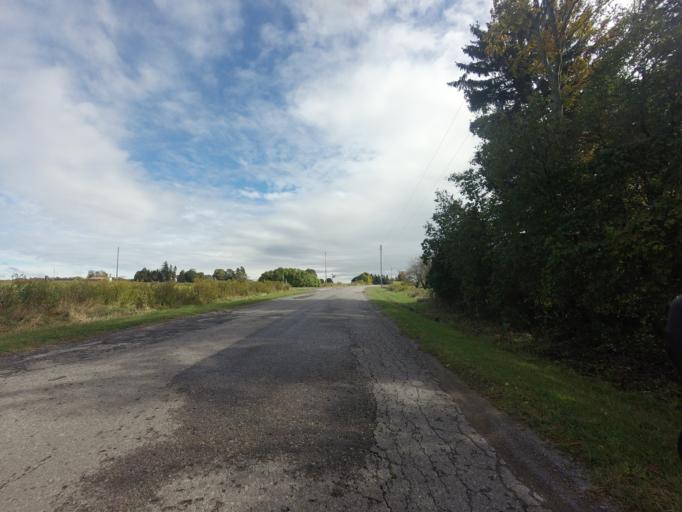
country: CA
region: Ontario
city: Cobourg
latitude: 43.9379
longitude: -78.3573
